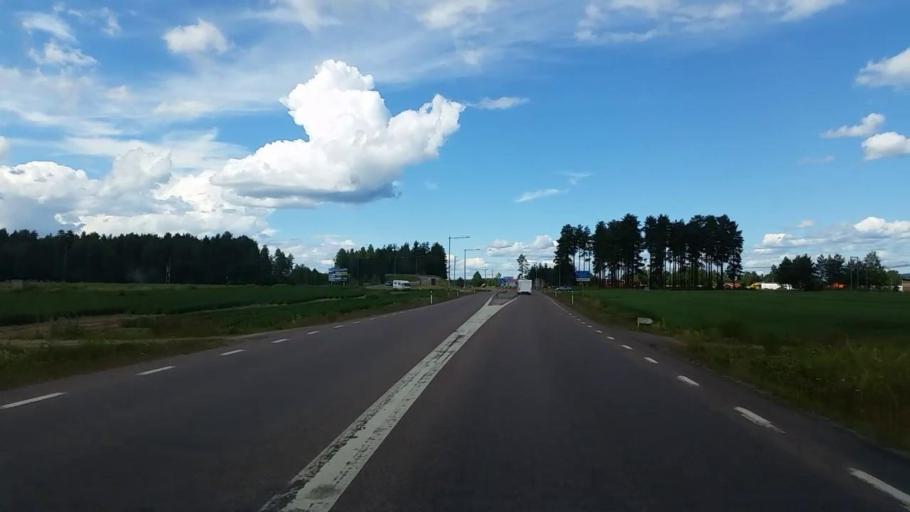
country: SE
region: Dalarna
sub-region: Leksand Municipality
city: Leksand
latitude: 60.7176
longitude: 15.0249
